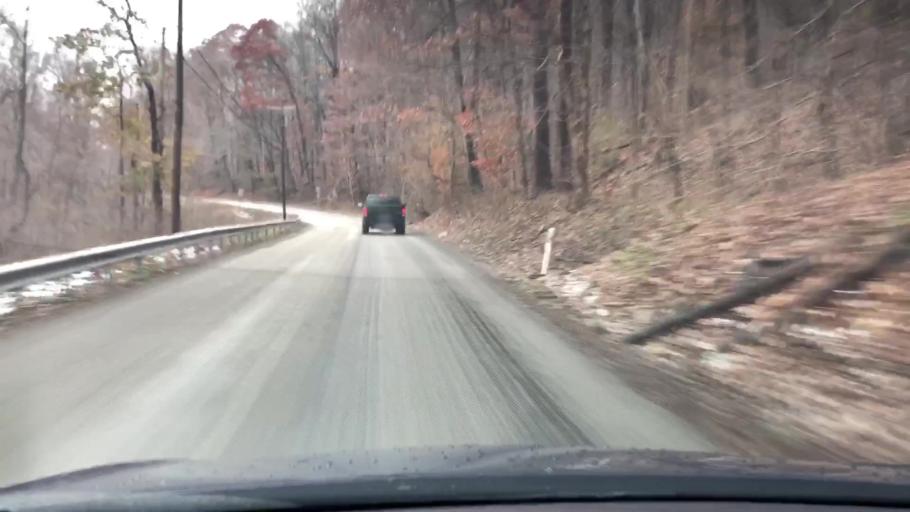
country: US
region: Pennsylvania
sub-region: Fayette County
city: Dunbar
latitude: 39.9671
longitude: -79.5898
